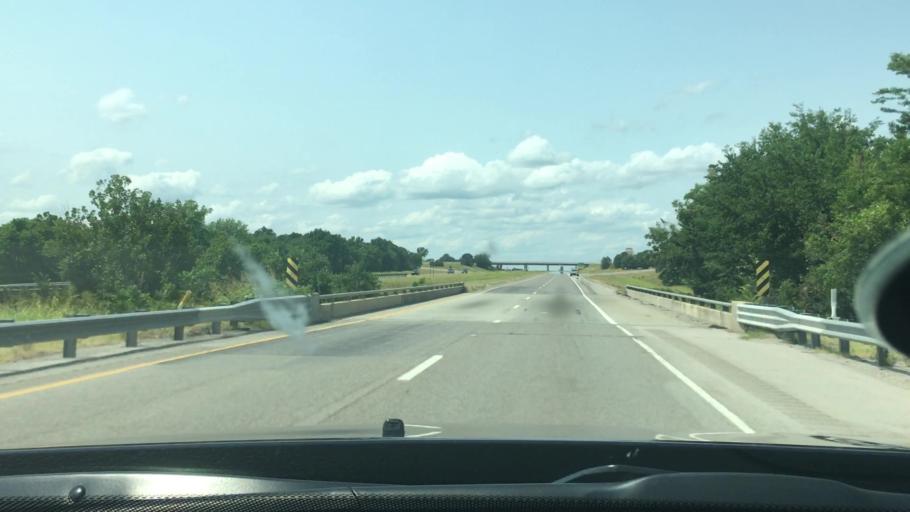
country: US
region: Oklahoma
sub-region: Murray County
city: Davis
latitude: 34.5005
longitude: -97.1700
